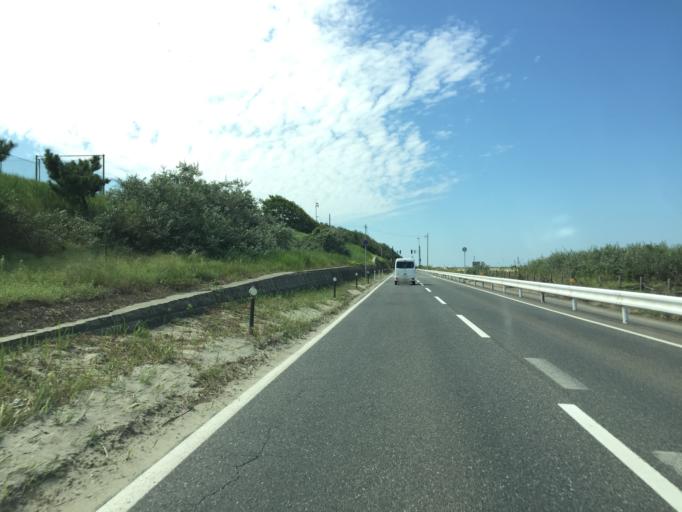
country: JP
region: Niigata
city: Niigata-shi
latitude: 37.9367
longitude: 139.0484
